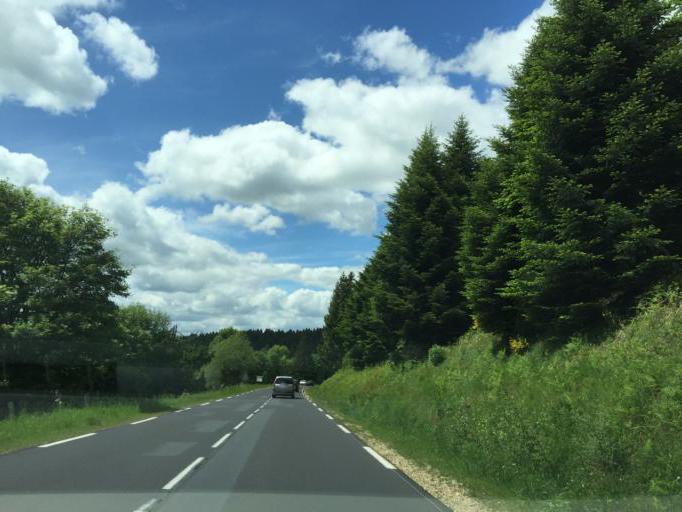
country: FR
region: Auvergne
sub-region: Departement du Puy-de-Dome
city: Ambert
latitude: 45.5225
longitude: 3.8323
